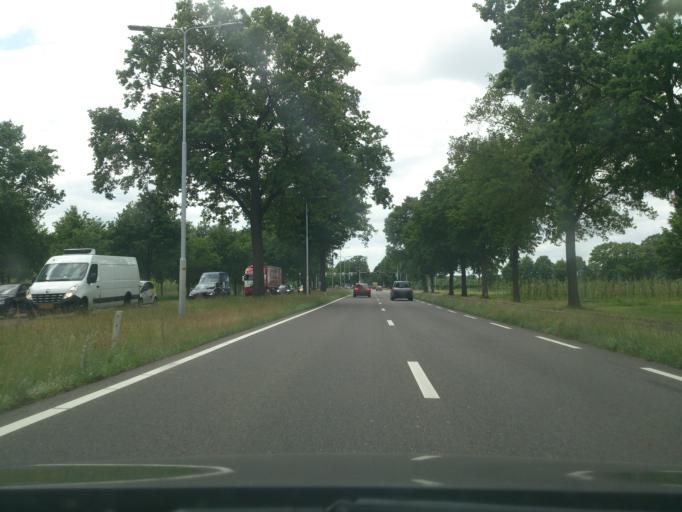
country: NL
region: North Brabant
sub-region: Gemeente Haaren
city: Haaren
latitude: 51.6152
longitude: 5.2088
